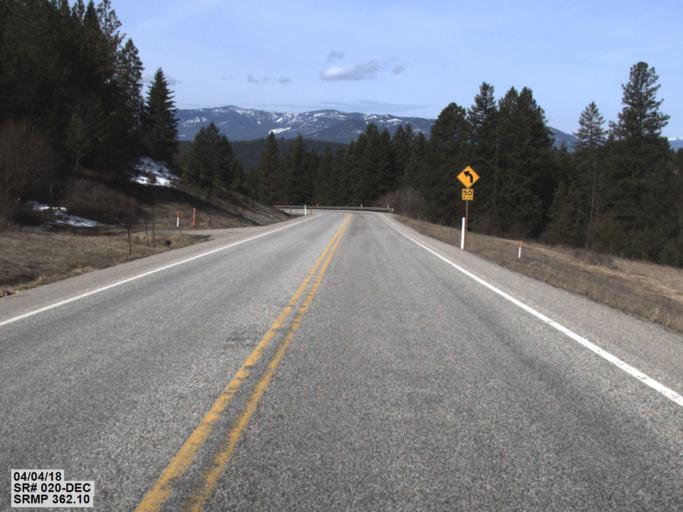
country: US
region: Washington
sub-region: Stevens County
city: Colville
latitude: 48.5160
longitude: -117.7669
